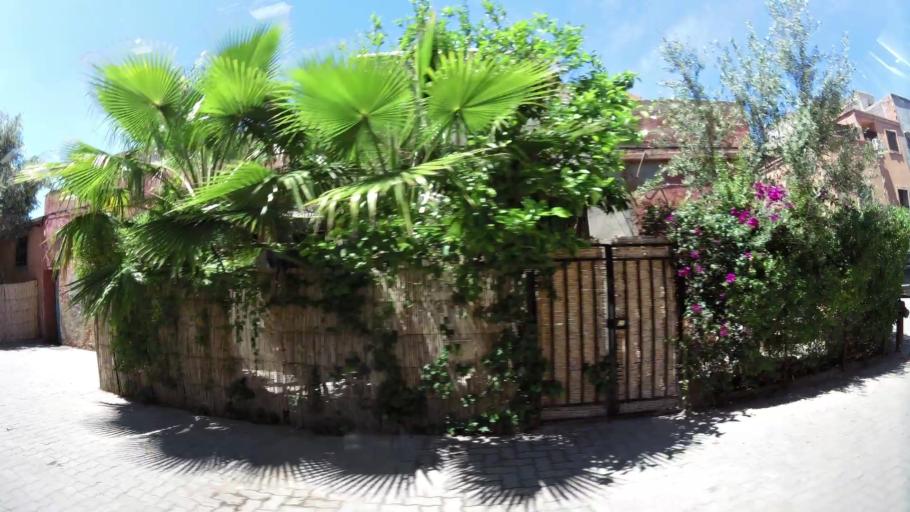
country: MA
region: Marrakech-Tensift-Al Haouz
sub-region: Marrakech
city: Marrakesh
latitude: 31.6288
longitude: -8.0431
